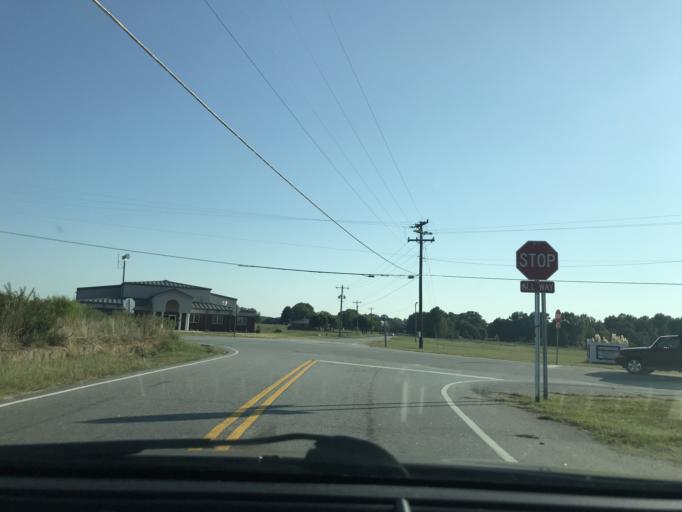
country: US
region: South Carolina
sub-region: Cherokee County
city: Gaffney
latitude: 35.1465
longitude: -81.7462
